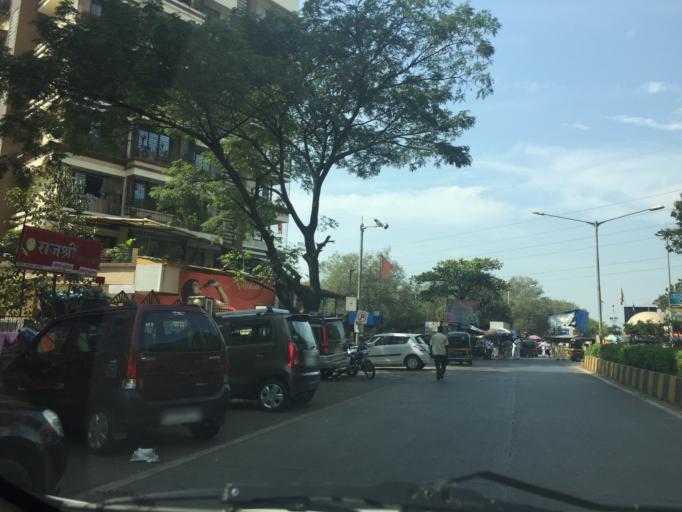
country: IN
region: Maharashtra
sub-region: Mumbai Suburban
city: Borivli
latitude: 19.2330
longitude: 72.8252
